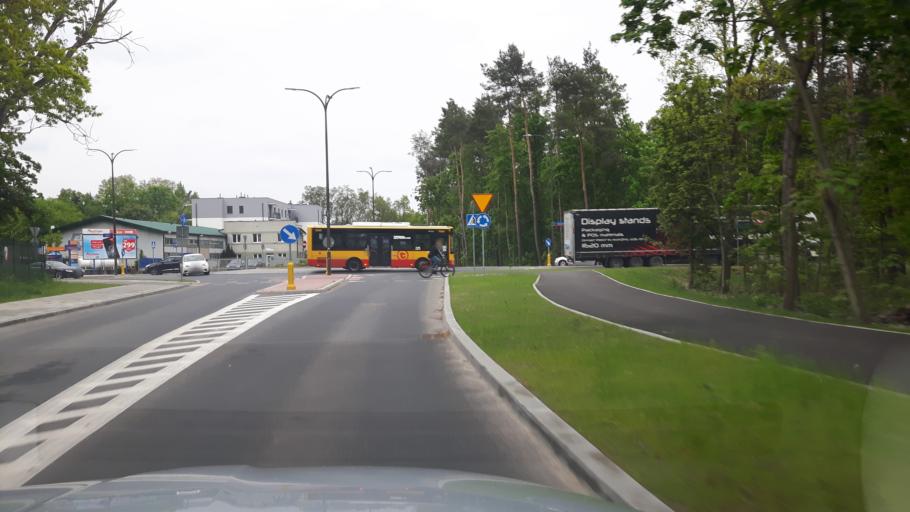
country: PL
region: Masovian Voivodeship
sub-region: Warszawa
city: Rembertow
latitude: 52.2613
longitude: 21.1510
